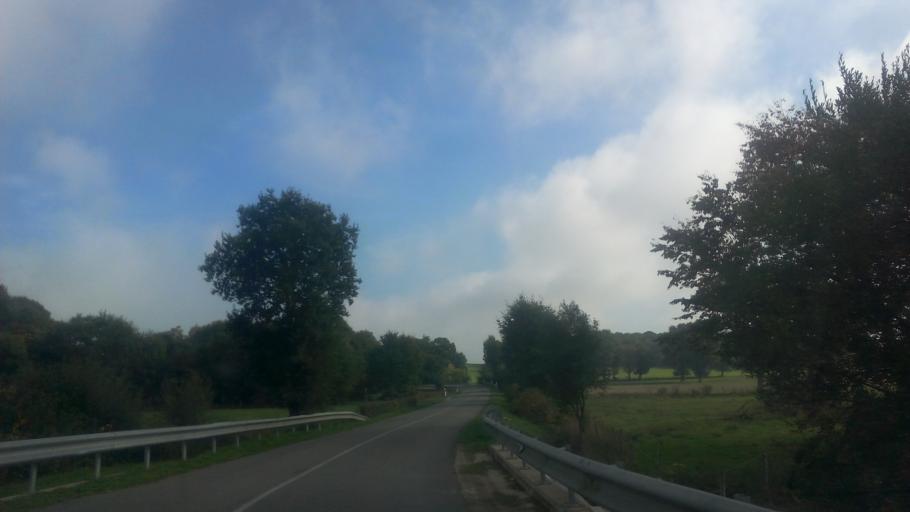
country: FR
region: Pays de la Loire
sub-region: Departement de la Loire-Atlantique
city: Conquereuil
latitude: 47.6253
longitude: -1.7677
